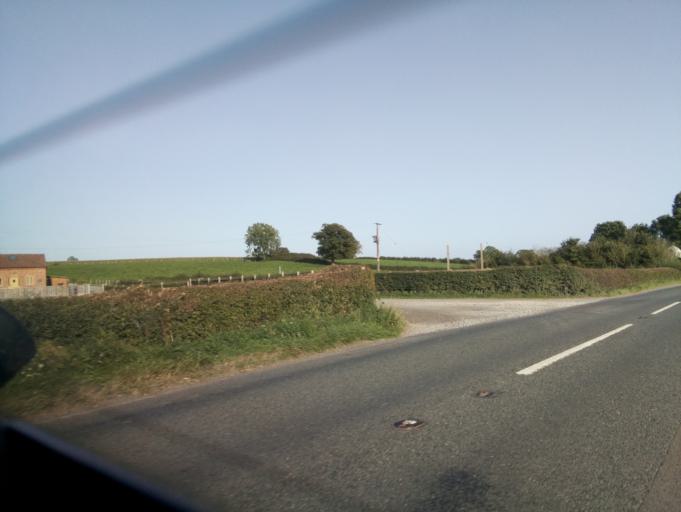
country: GB
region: England
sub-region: Gloucestershire
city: Gloucester
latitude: 51.9599
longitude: -2.2510
